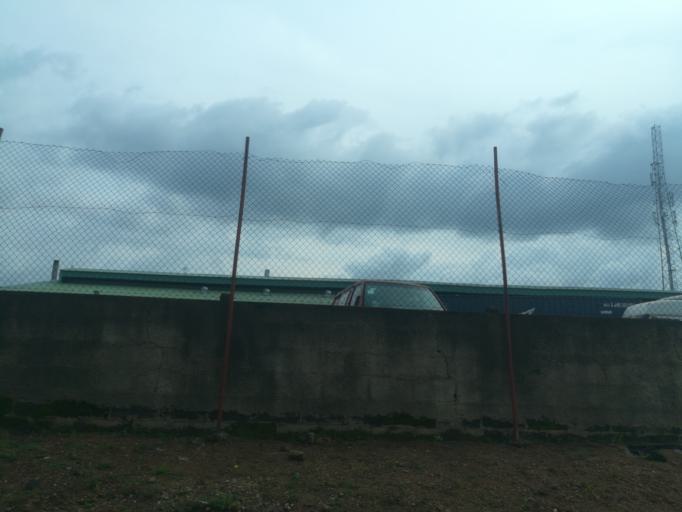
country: NG
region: Oyo
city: Ibadan
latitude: 7.3674
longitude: 3.8539
